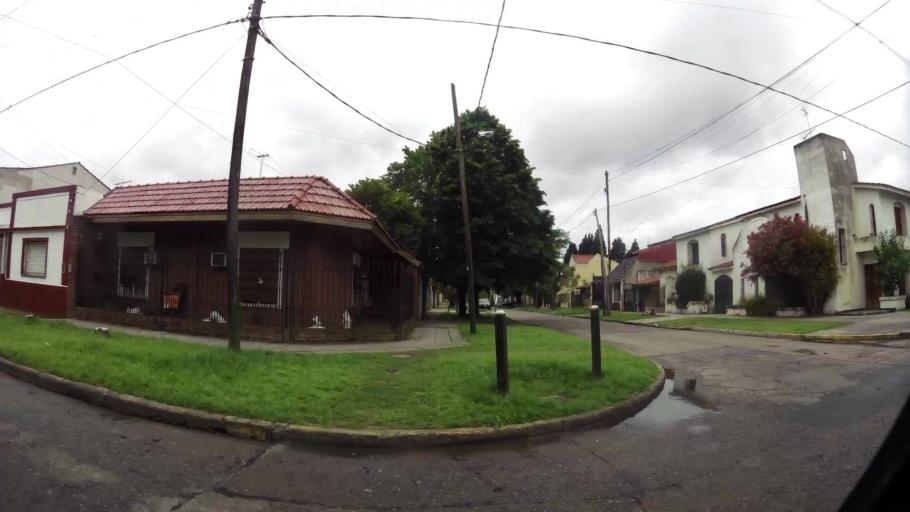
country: AR
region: Buenos Aires
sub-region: Partido de Lomas de Zamora
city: Lomas de Zamora
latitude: -34.7538
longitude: -58.3853
